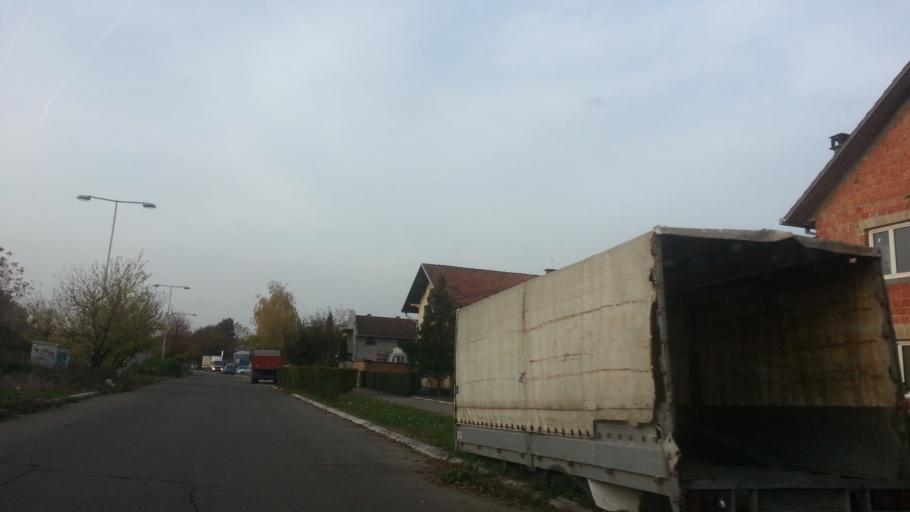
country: RS
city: Novi Banovci
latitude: 44.8960
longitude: 20.2809
